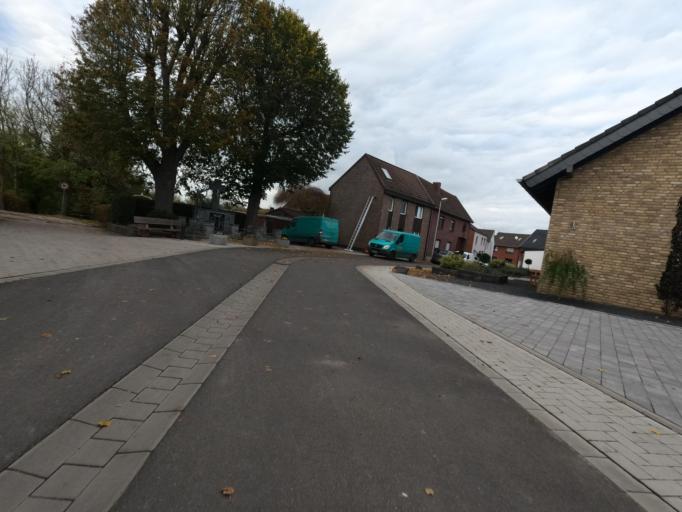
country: DE
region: North Rhine-Westphalia
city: Geilenkirchen
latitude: 50.9888
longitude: 6.1686
